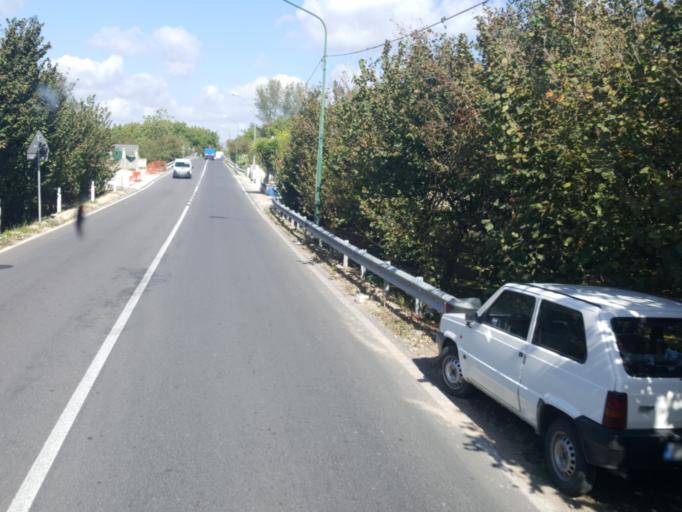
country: IT
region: Campania
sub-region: Provincia di Napoli
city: Nola
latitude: 40.9223
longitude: 14.5128
